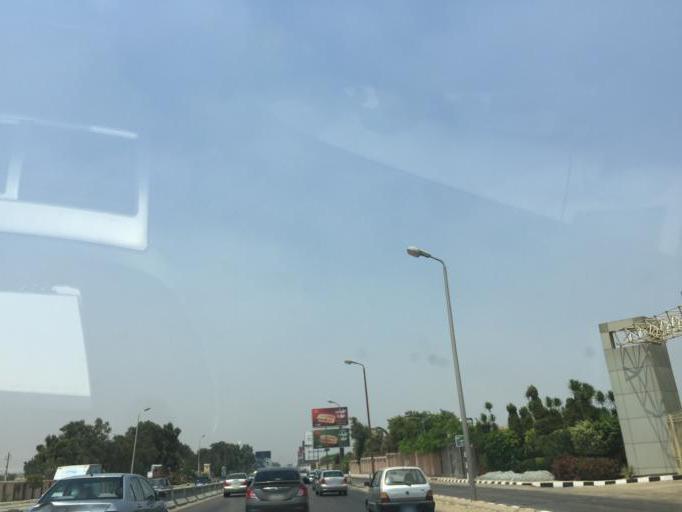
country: EG
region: Muhafazat al Qalyubiyah
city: Al Khankah
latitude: 30.0814
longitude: 31.4071
